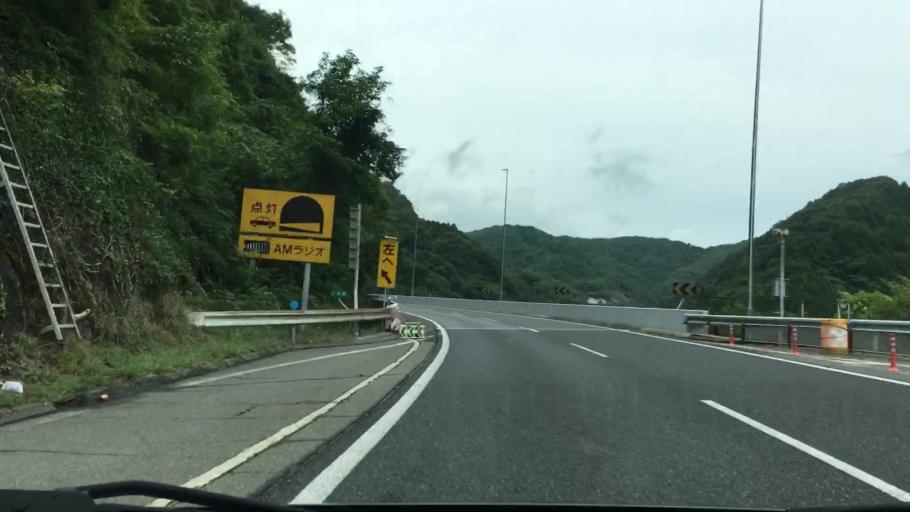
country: JP
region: Okayama
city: Niimi
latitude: 34.9957
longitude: 133.6055
